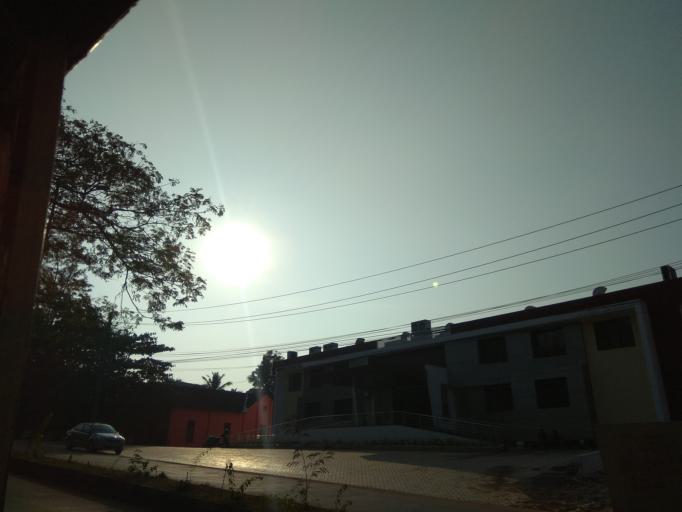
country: IN
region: Karnataka
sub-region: Dakshina Kannada
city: Mangalore
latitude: 12.9042
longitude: 74.8461
